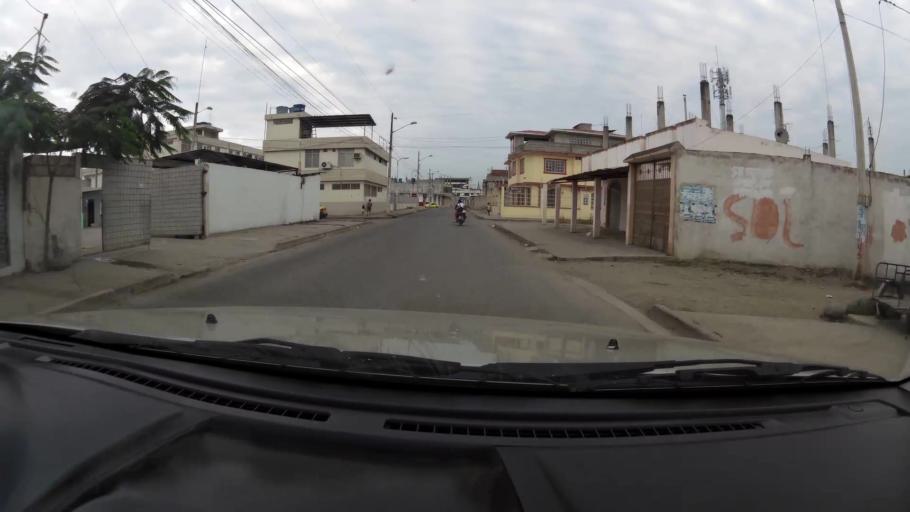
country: EC
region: El Oro
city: Machala
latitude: -3.2474
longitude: -79.9620
